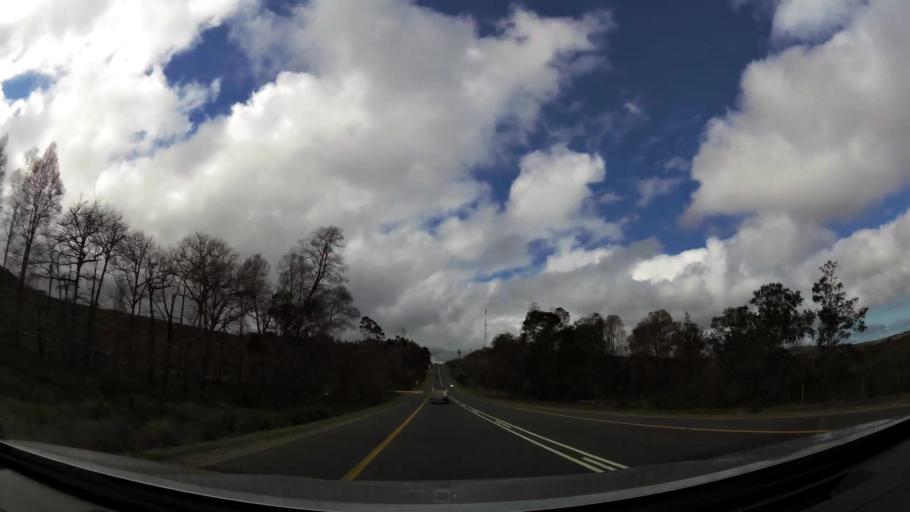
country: ZA
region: Western Cape
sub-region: Eden District Municipality
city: Knysna
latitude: -34.0378
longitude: 23.1398
